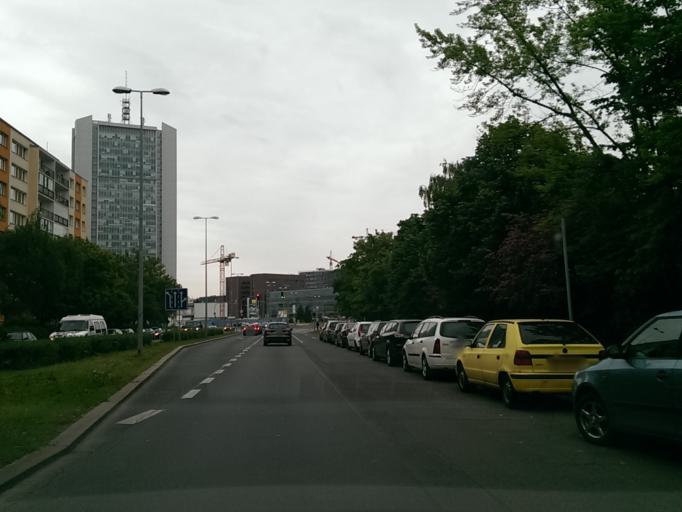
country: CZ
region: Praha
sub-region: Praha 2
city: Vysehrad
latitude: 50.0472
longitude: 14.4397
